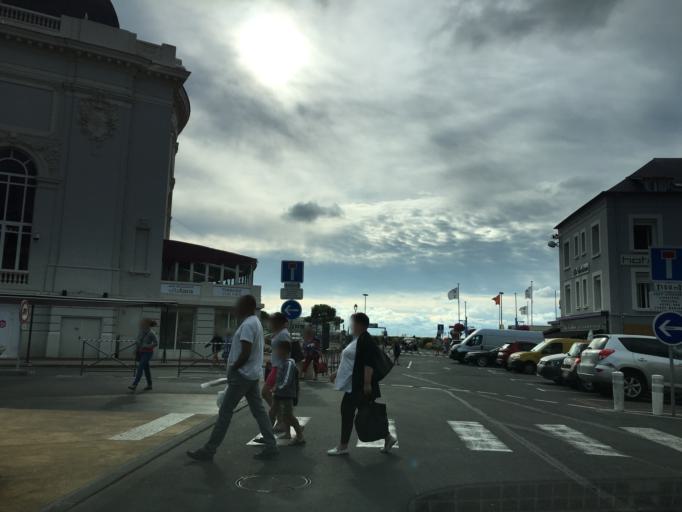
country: FR
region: Lower Normandy
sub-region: Departement du Calvados
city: Trouville-sur-Mer
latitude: 49.3664
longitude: 0.0789
